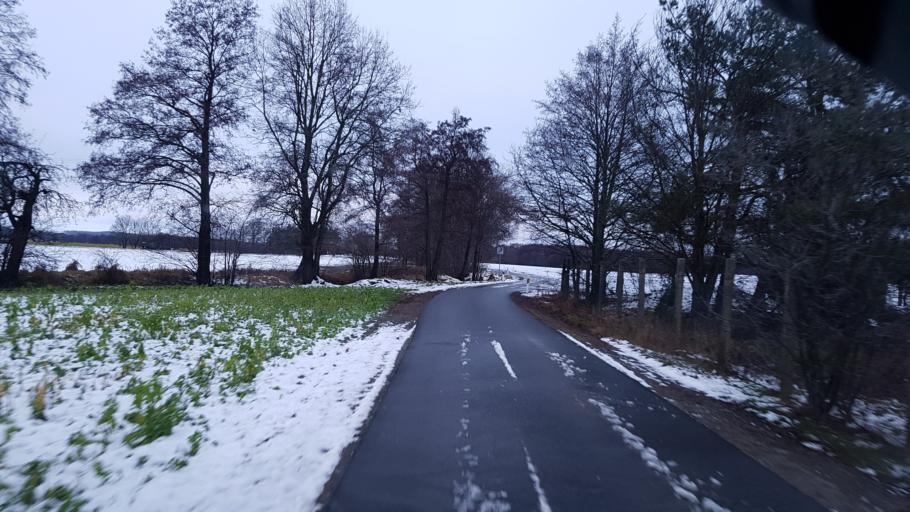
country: DE
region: Brandenburg
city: Luckau
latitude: 51.7755
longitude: 13.6929
